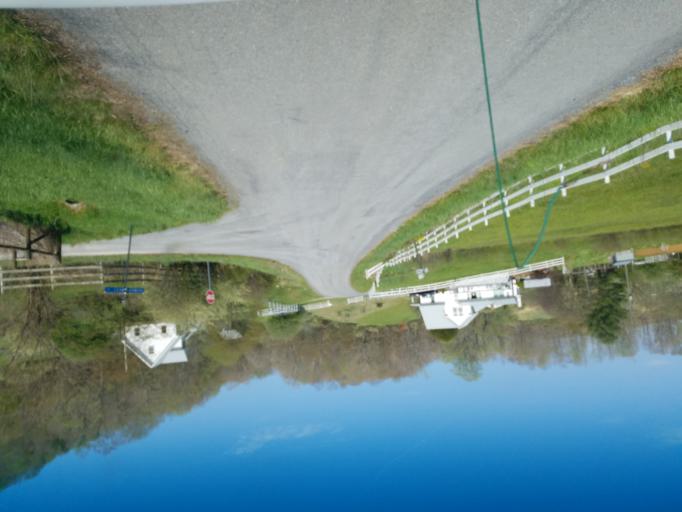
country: US
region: Virginia
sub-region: Smyth County
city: Marion
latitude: 36.7579
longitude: -81.4706
